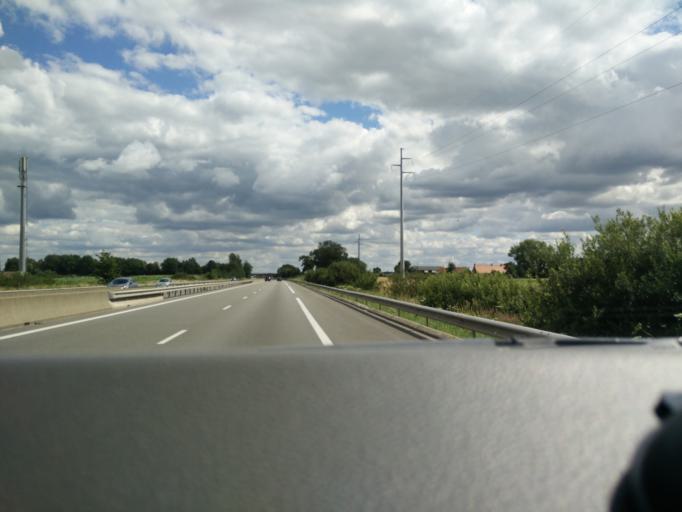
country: FR
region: Nord-Pas-de-Calais
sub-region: Departement du Nord
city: Herzeele
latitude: 50.8721
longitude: 2.5281
